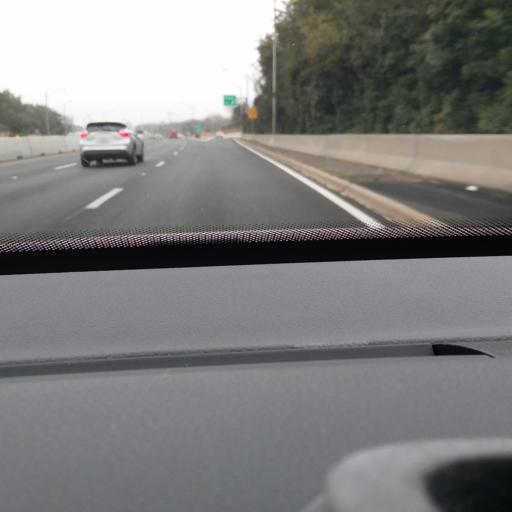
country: US
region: Texas
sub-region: Dallas County
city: University Park
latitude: 32.8611
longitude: -96.7933
